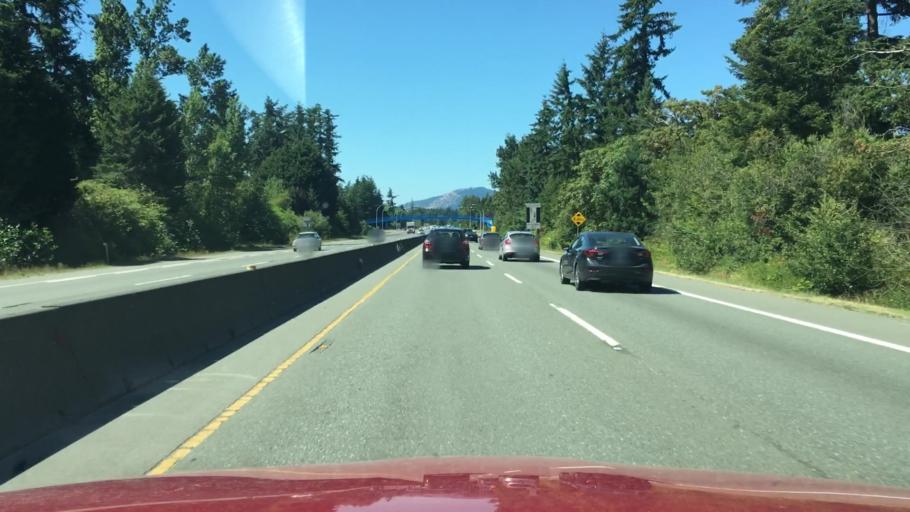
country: CA
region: British Columbia
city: North Saanich
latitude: 48.6126
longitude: -123.4014
